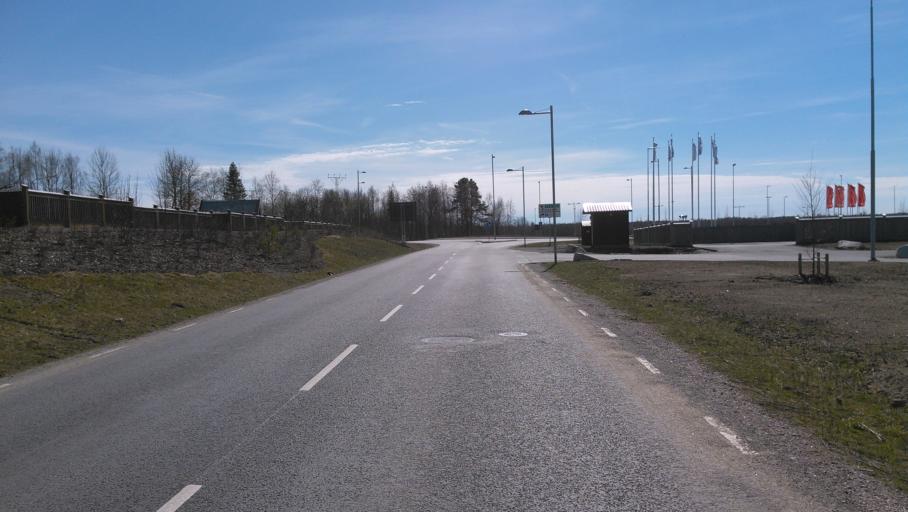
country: SE
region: Vaesterbotten
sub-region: Umea Kommun
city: Umea
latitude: 63.8060
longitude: 20.2573
